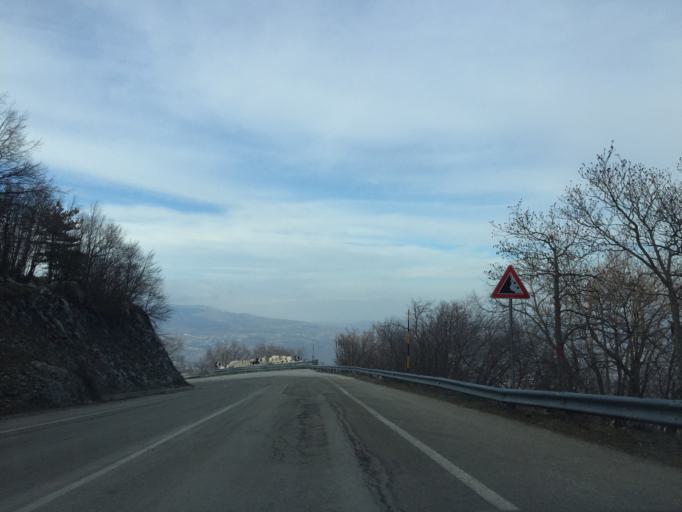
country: IT
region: Molise
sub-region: Provincia di Campobasso
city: San Massimo
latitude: 41.4731
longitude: 14.4149
